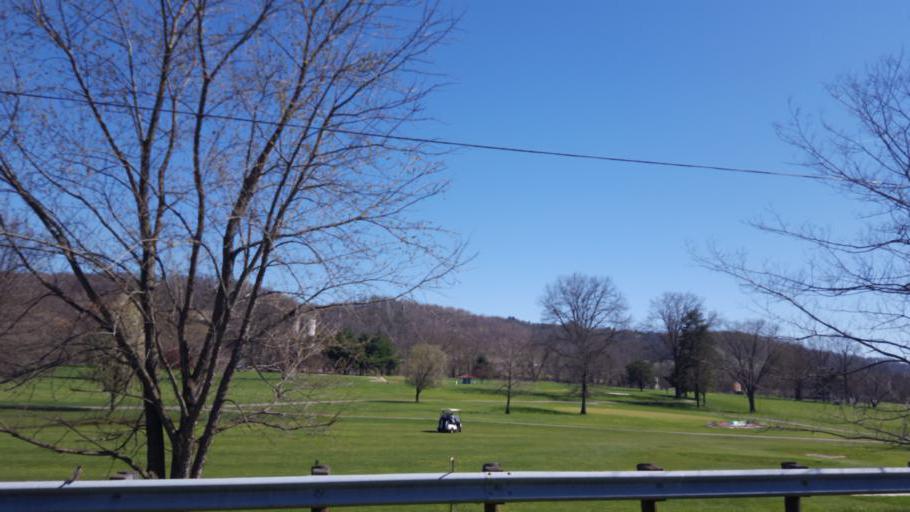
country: US
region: Ohio
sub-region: Jefferson County
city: Tiltonsville
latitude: 40.1803
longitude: -80.6911
